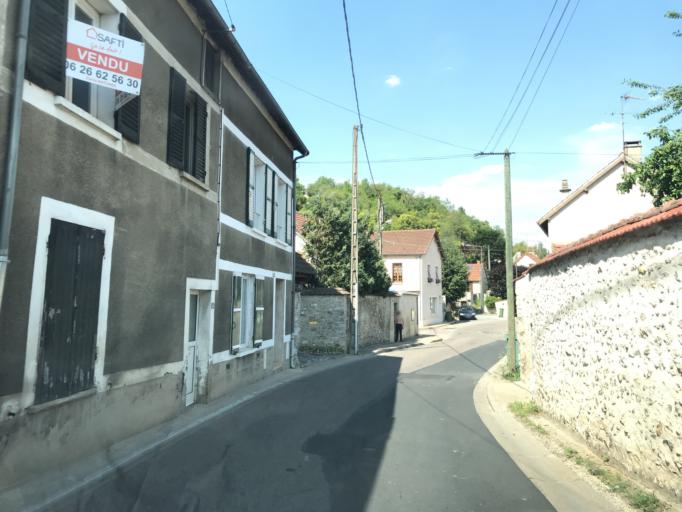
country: FR
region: Ile-de-France
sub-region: Departement des Yvelines
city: Freneuse
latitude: 49.0517
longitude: 1.5897
